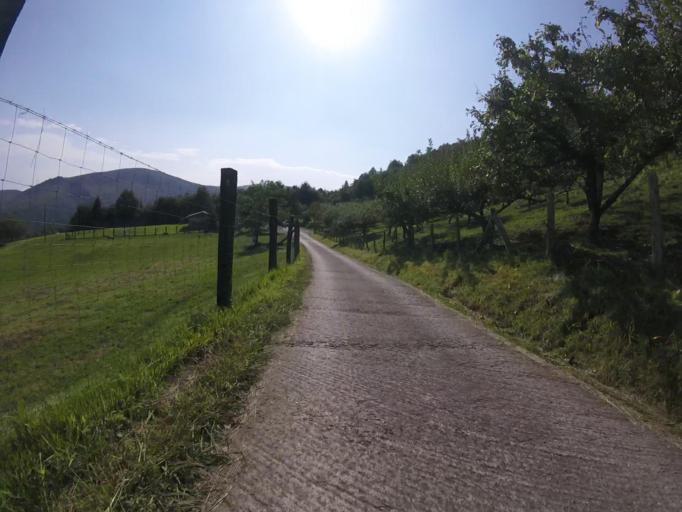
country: ES
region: Basque Country
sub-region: Provincia de Guipuzcoa
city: Irun
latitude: 43.3271
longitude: -1.7580
